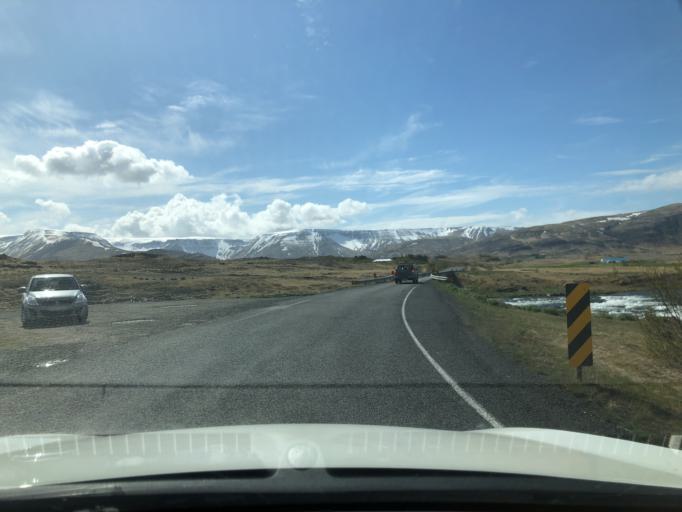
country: IS
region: Capital Region
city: Mosfellsbaer
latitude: 64.3417
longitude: -21.6082
